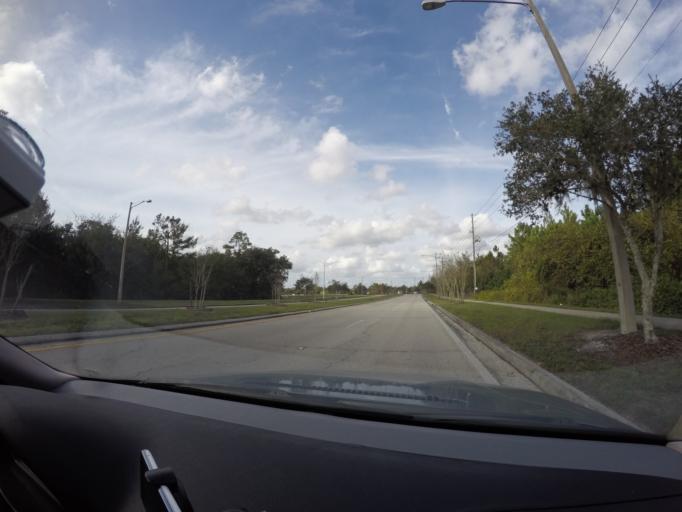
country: US
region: Florida
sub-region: Orange County
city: Conway
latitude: 28.4105
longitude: -81.2095
